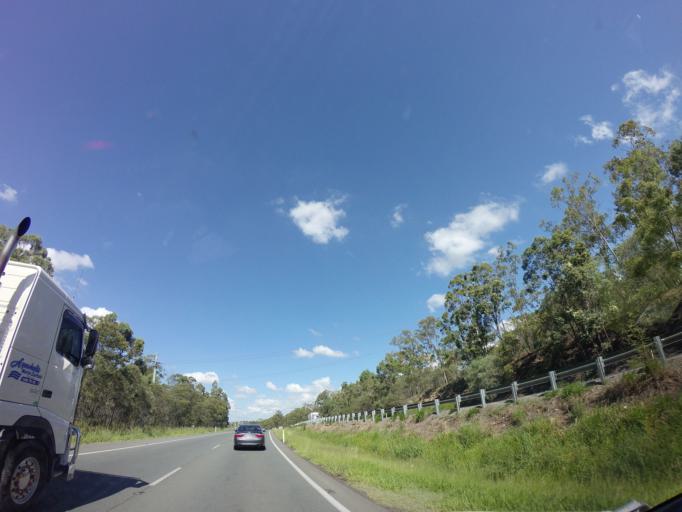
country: AU
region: Queensland
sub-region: Ipswich
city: Tivoli
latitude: -27.5805
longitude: 152.7660
